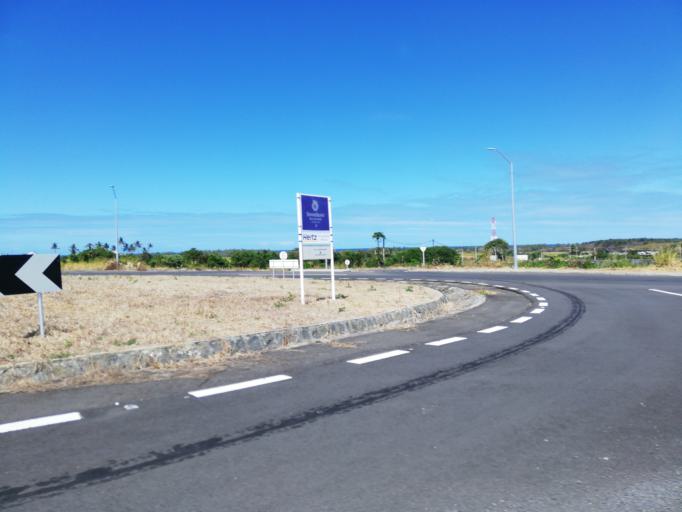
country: MU
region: Grand Port
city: Plaine Magnien
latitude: -20.4425
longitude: 57.6899
